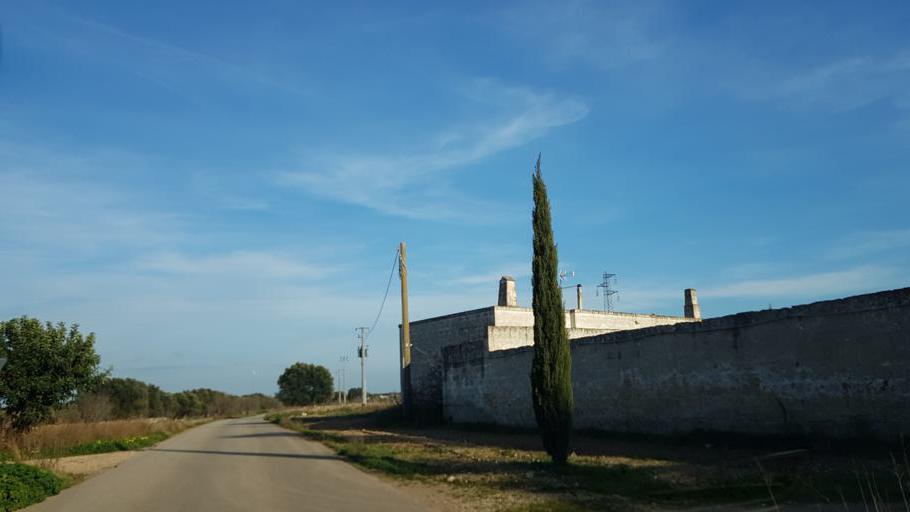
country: IT
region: Apulia
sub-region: Provincia di Brindisi
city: San Vito dei Normanni
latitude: 40.6648
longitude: 17.7823
